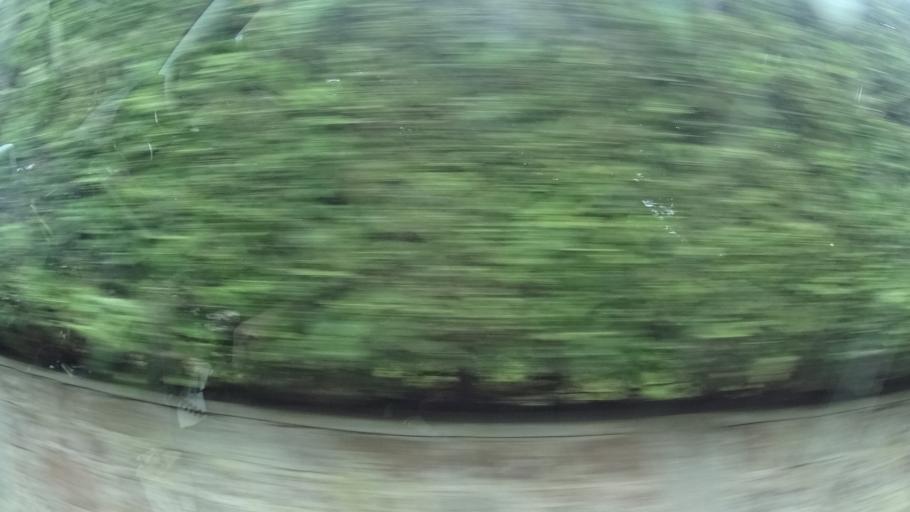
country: DE
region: Bavaria
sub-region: Regierungsbezirk Unterfranken
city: Wartmannsroth
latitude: 50.1452
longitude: 9.7787
